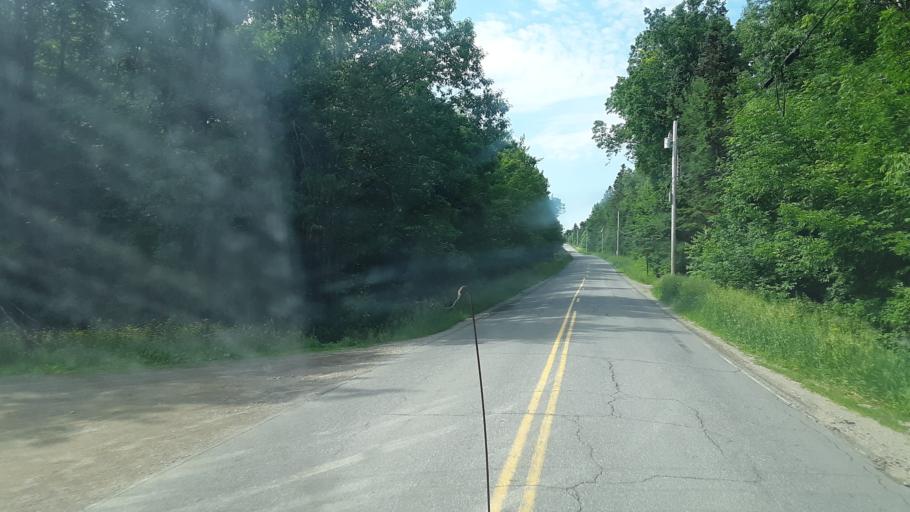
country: US
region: Maine
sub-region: Waldo County
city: Frankfort
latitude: 44.5852
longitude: -68.9458
